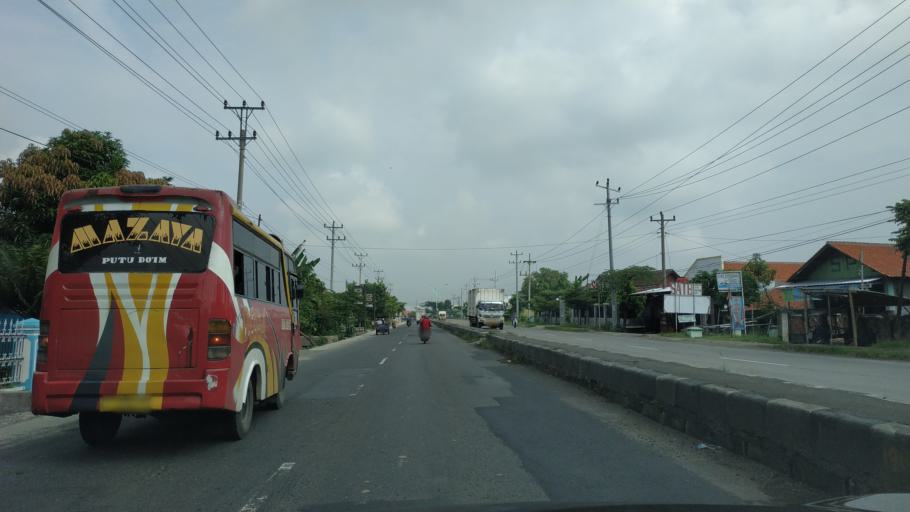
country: ID
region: Central Java
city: Bulakamba
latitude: -6.8735
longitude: 108.9134
